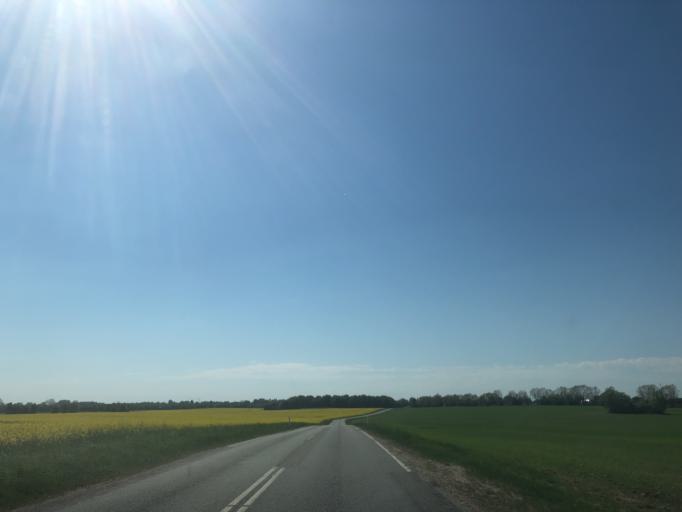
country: DK
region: Zealand
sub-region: Greve Kommune
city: Tune
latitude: 55.6262
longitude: 12.2106
